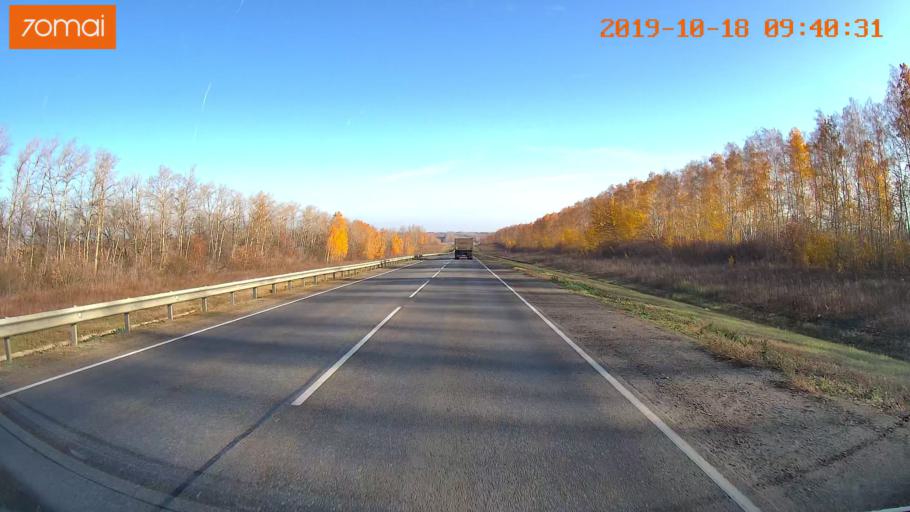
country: RU
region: Tula
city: Yefremov
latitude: 53.2649
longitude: 38.1493
